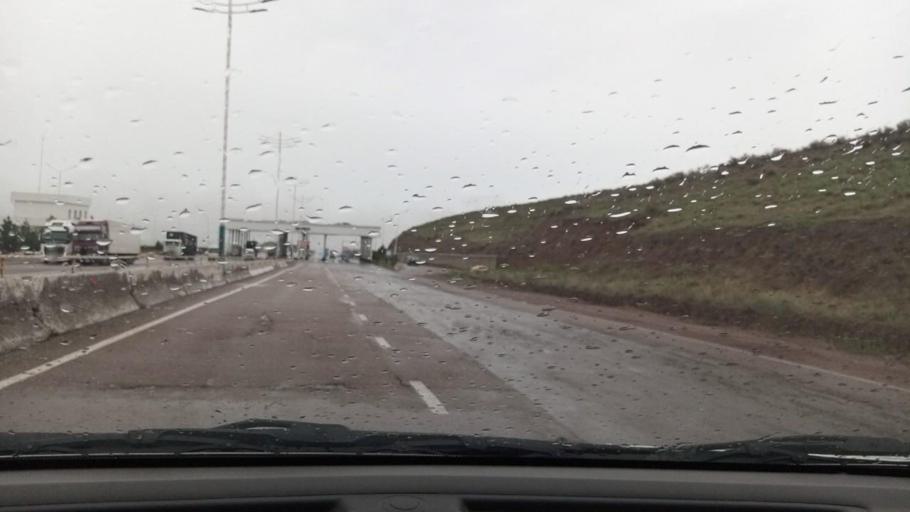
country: UZ
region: Namangan
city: Pop Shahri
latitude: 40.9231
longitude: 70.7322
